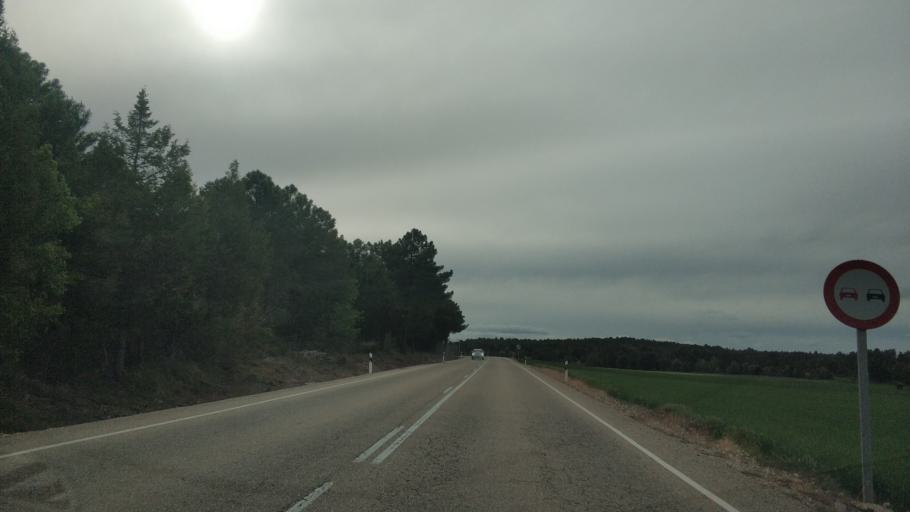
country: ES
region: Castille and Leon
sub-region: Provincia de Soria
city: Bayubas de Abajo
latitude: 41.5071
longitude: -2.9053
